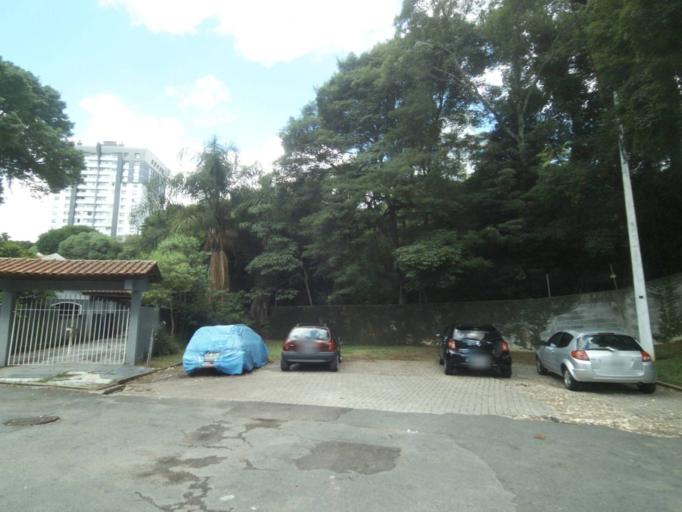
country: BR
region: Parana
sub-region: Curitiba
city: Curitiba
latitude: -25.4370
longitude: -49.3318
